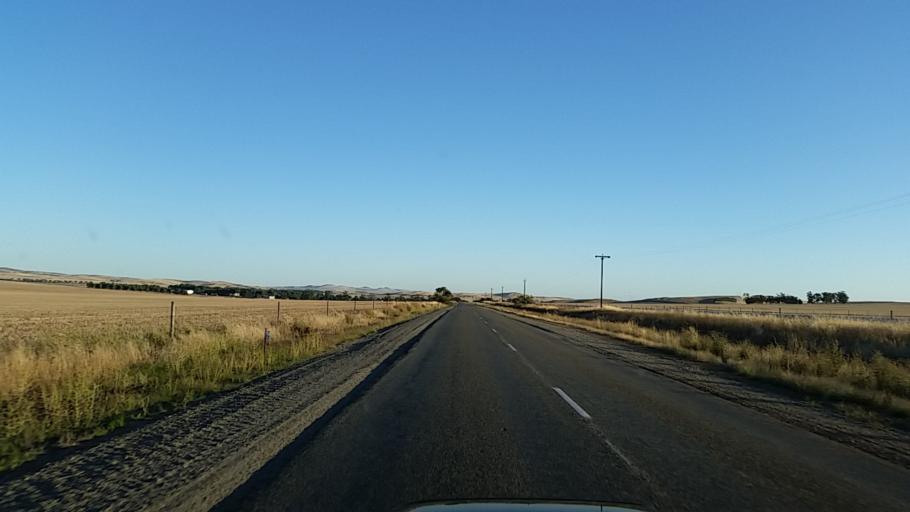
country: AU
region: South Australia
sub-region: Northern Areas
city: Jamestown
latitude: -33.4809
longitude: 138.5975
